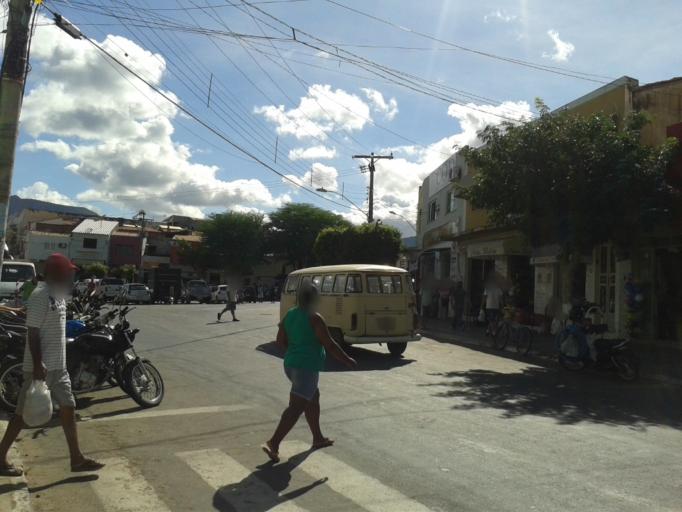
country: BR
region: Bahia
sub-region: Livramento Do Brumado
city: Livramento do Brumado
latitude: -13.6487
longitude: -41.8421
